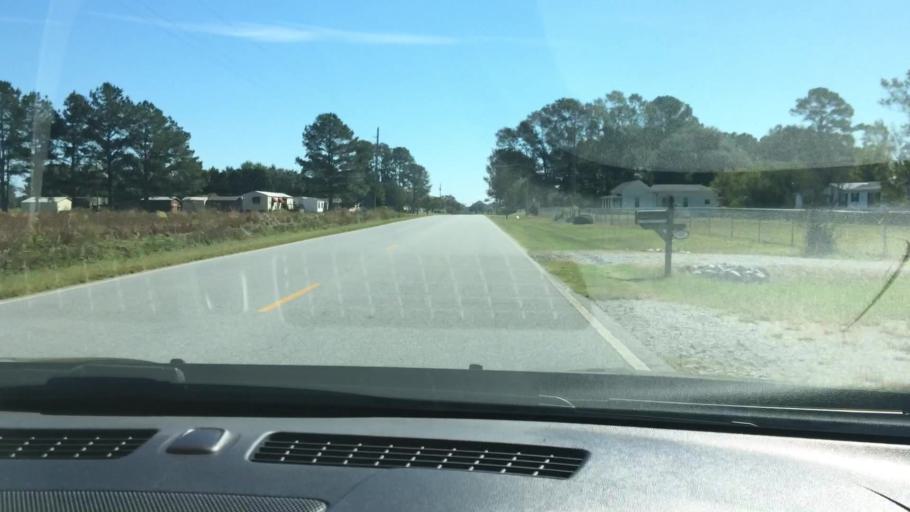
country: US
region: North Carolina
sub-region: Pitt County
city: Grifton
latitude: 35.3889
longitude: -77.3848
